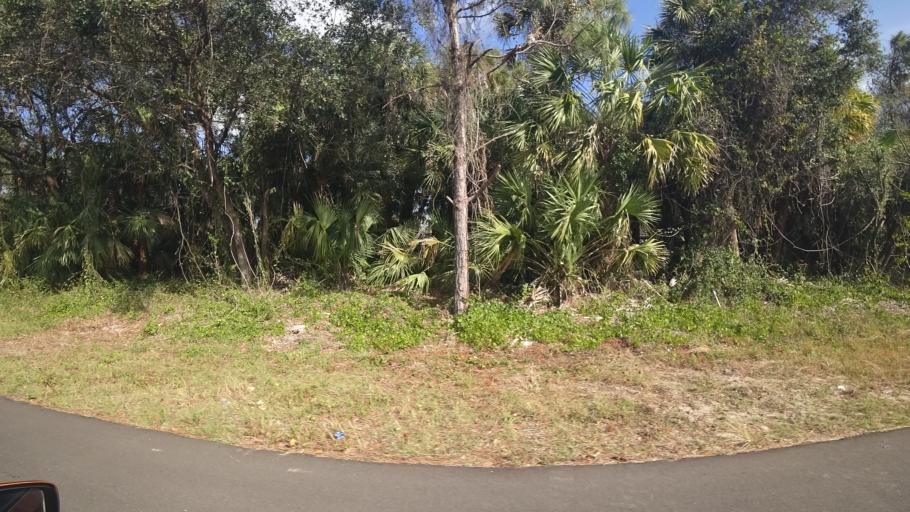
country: US
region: Florida
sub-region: Charlotte County
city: Port Charlotte
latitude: 27.0534
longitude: -82.1205
